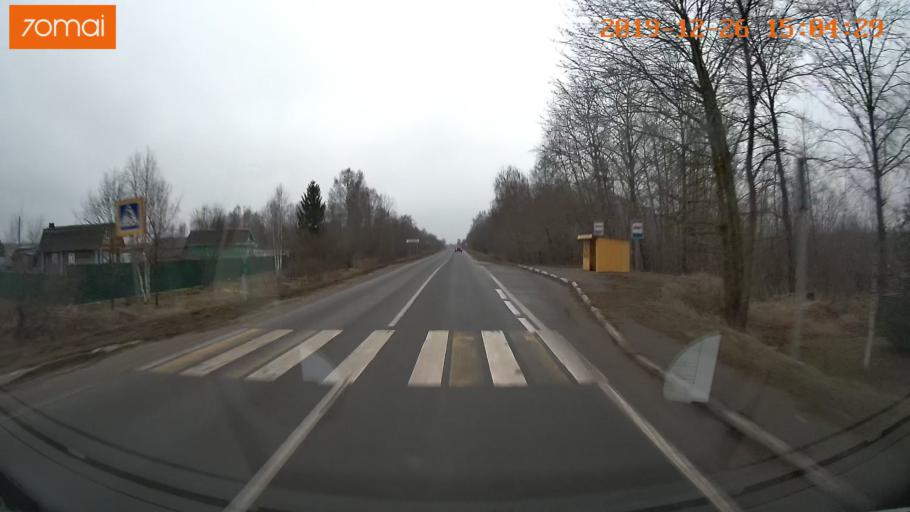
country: RU
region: Jaroslavl
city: Rybinsk
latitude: 58.1993
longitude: 38.8613
